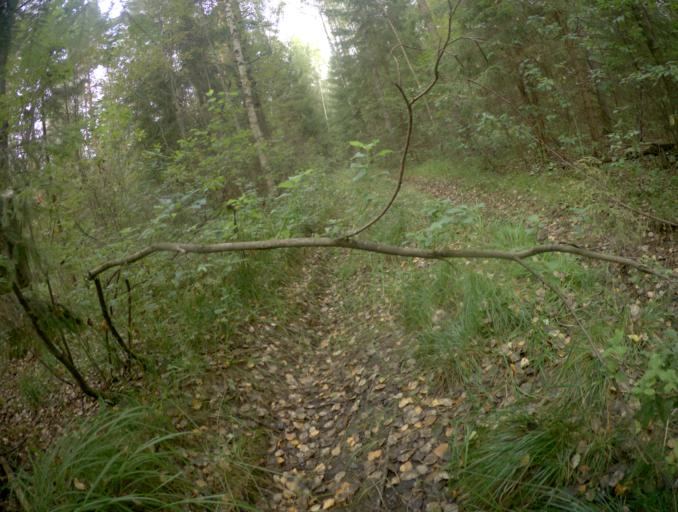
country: RU
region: Vladimir
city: Golovino
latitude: 55.9129
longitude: 40.4985
